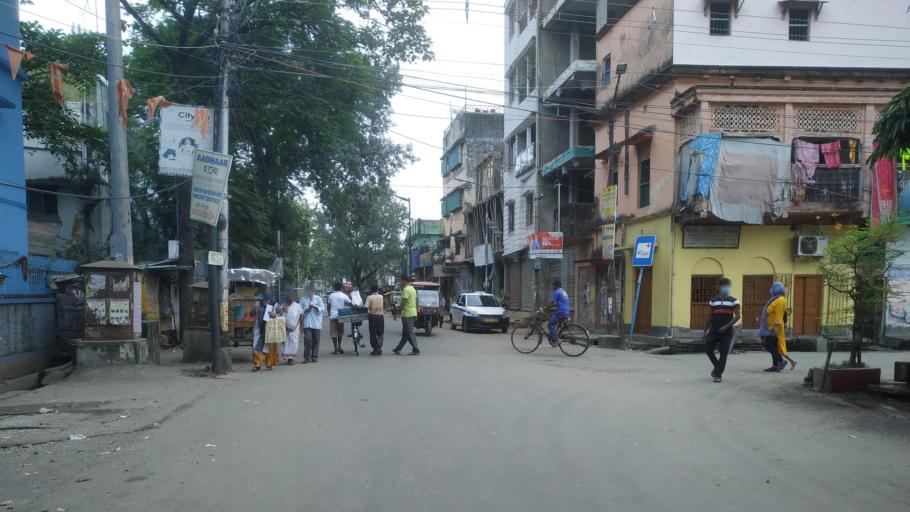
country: IN
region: West Bengal
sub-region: North 24 Parganas
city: Dam Dam
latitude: 22.6385
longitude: 88.4152
